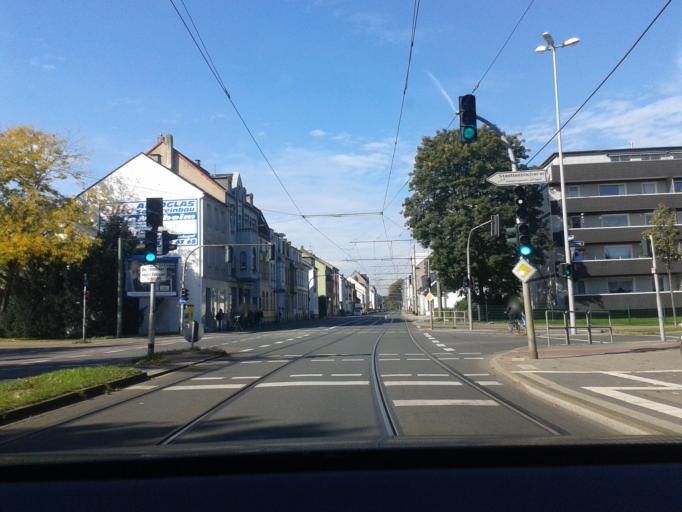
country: DE
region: North Rhine-Westphalia
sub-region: Regierungsbezirk Dusseldorf
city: Muelheim (Ruhr)
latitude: 51.4290
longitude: 6.8403
